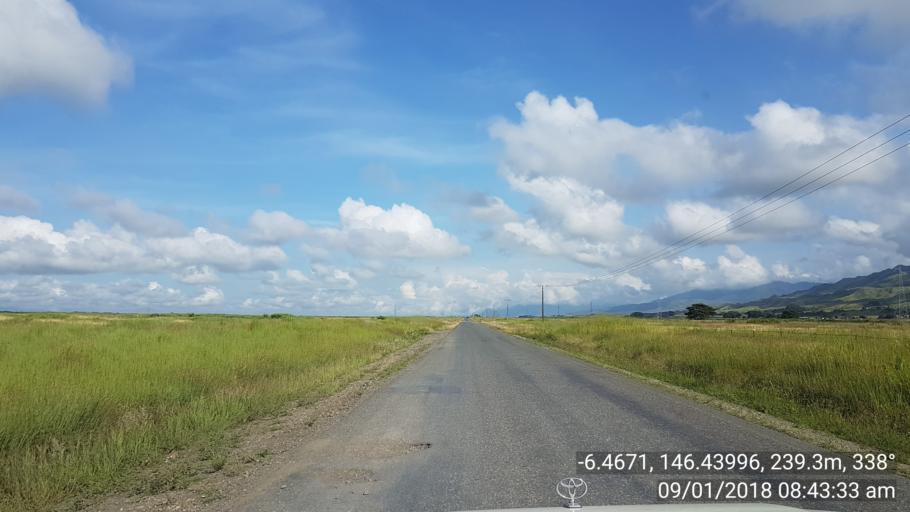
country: PG
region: Morobe
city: Lae
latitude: -6.4677
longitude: 146.4402
